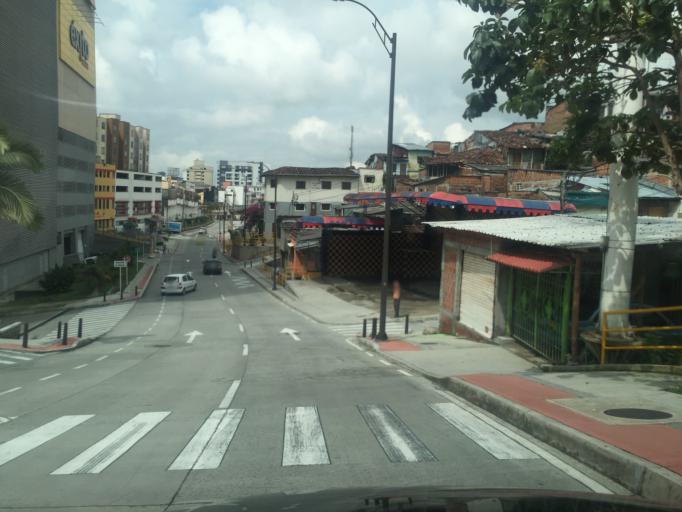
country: CO
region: Risaralda
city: Pereira
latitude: 4.8083
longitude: -75.6832
